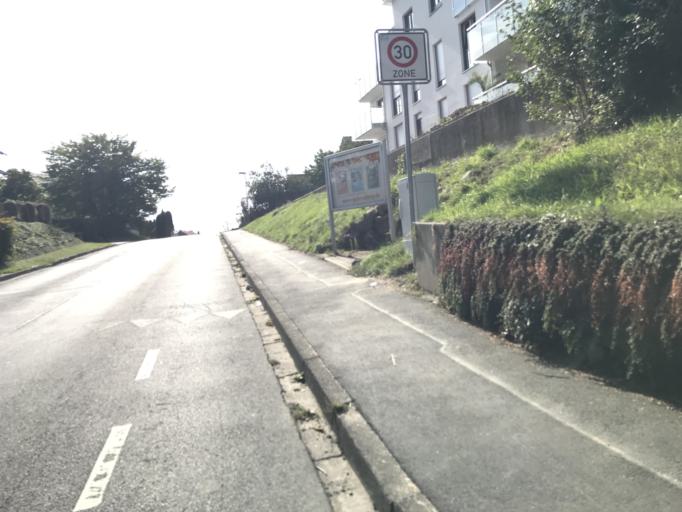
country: DE
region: Hesse
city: Gudensberg
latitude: 51.1751
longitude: 9.3622
